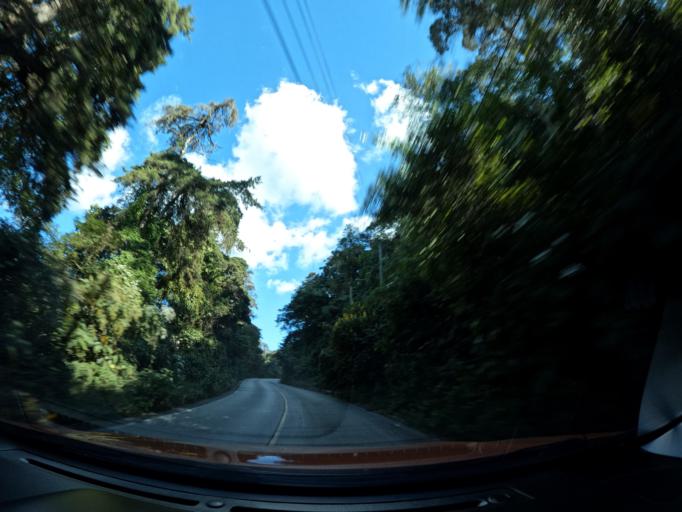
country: GT
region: Sacatepequez
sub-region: Municipio de Santa Maria de Jesus
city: Santa Maria de Jesus
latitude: 14.5126
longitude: -90.7215
